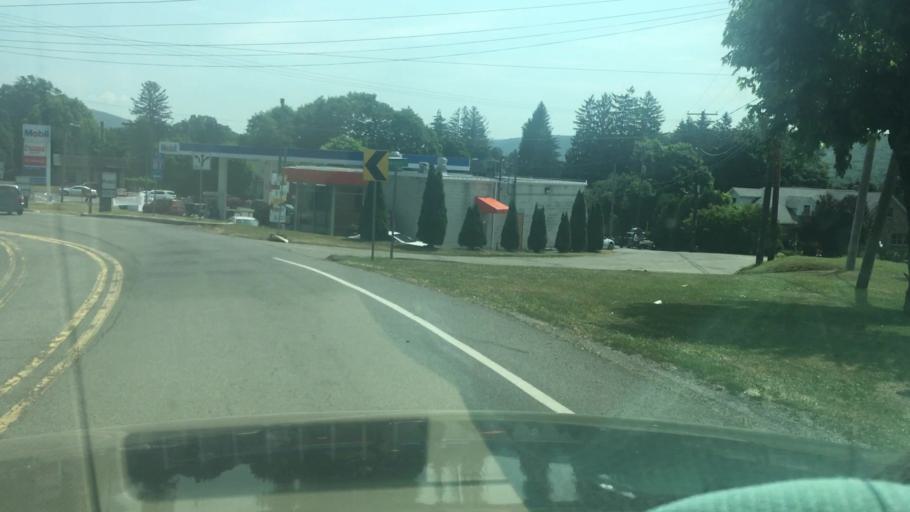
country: US
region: Pennsylvania
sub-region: Schuylkill County
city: Hometown
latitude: 40.8228
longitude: -75.9816
